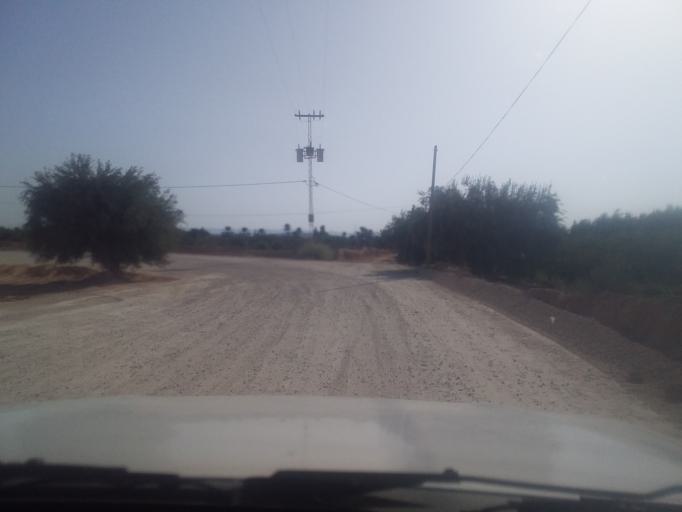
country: TN
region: Qabis
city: Matmata
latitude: 33.5979
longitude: 10.2736
